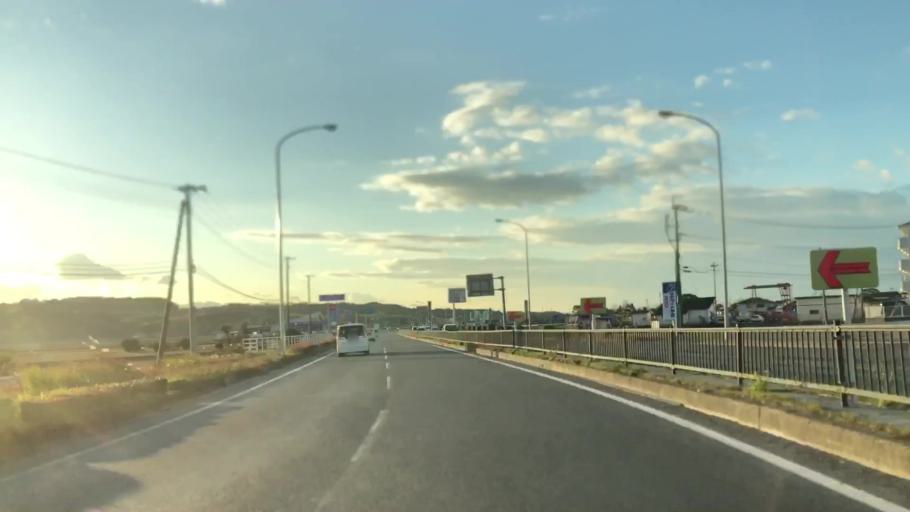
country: JP
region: Fukuoka
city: Nakatsu
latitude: 33.5511
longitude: 131.2736
